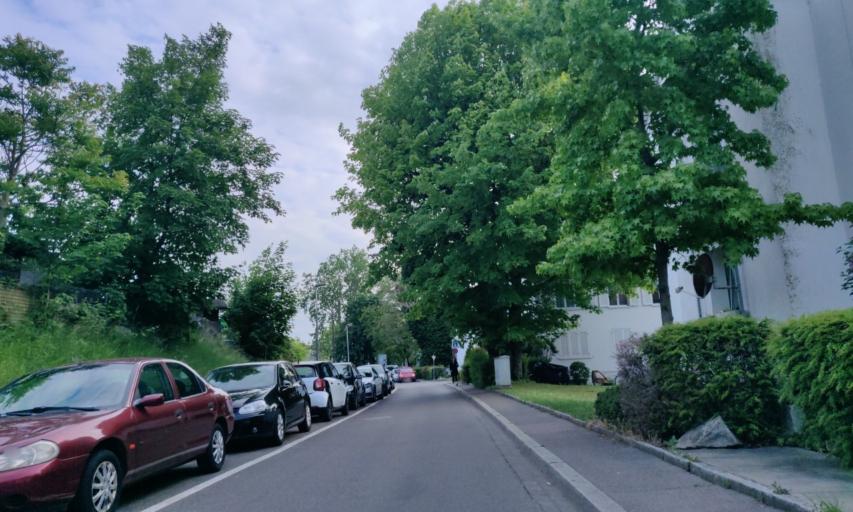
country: CH
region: Basel-Landschaft
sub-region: Bezirk Arlesheim
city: Birsfelden
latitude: 47.5639
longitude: 7.6277
